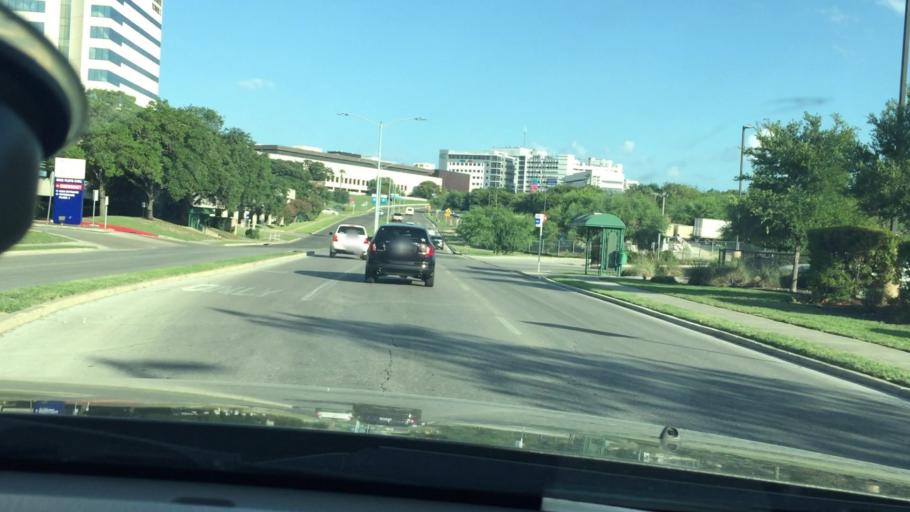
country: US
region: Texas
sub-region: Bexar County
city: Balcones Heights
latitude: 29.5131
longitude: -98.5777
